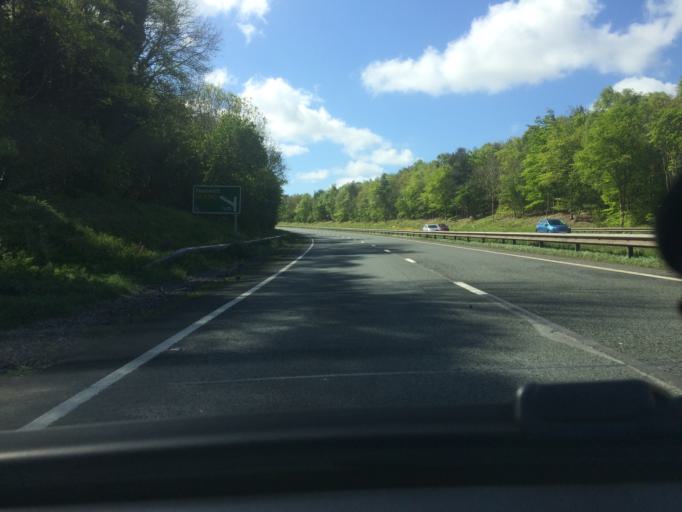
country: GB
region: Wales
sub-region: Wrexham
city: Gresford
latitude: 53.0855
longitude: -2.9874
